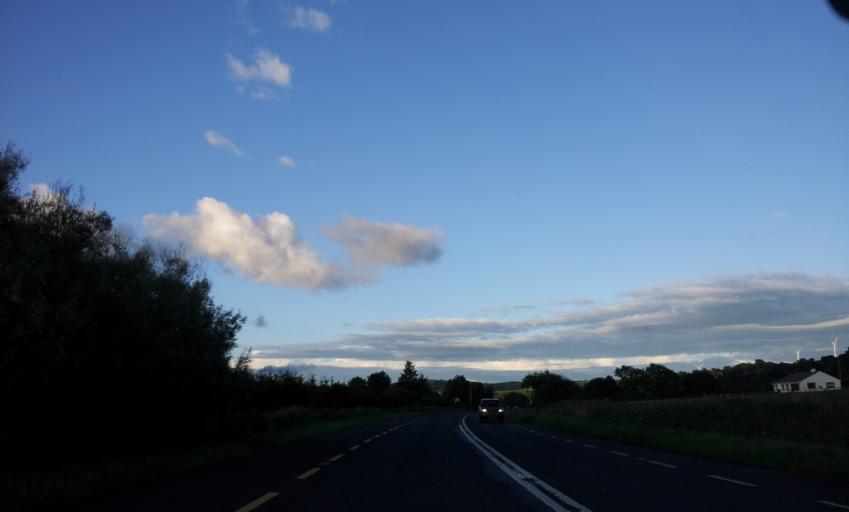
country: IE
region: Munster
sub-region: County Limerick
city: Abbeyfeale
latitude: 52.3882
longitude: -9.2013
